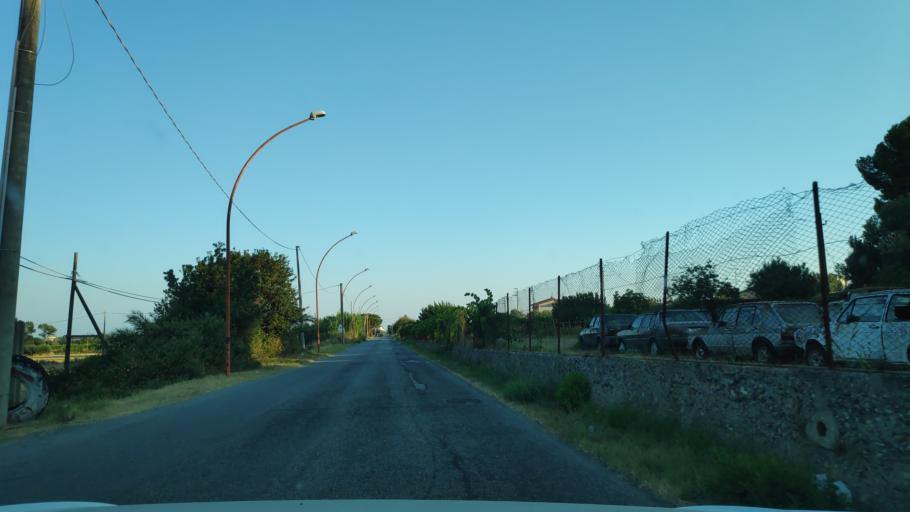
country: IT
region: Calabria
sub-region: Provincia di Reggio Calabria
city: Caulonia Marina
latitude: 38.3670
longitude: 16.4839
